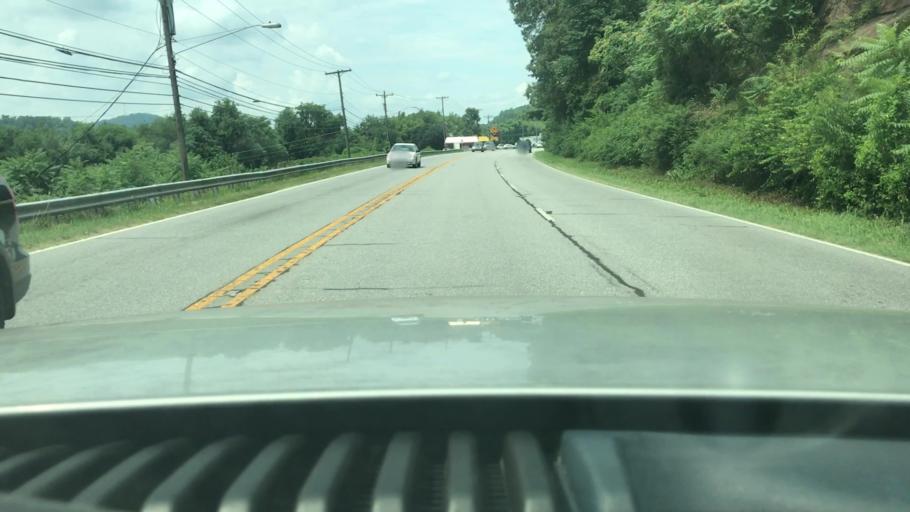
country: US
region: North Carolina
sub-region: Wilkes County
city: Wilkesboro
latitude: 36.1564
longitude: -81.1628
